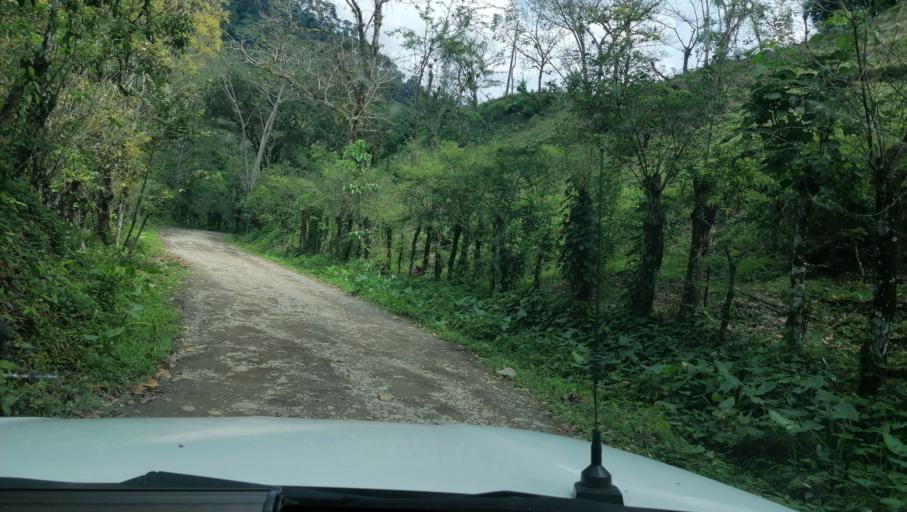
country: MX
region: Chiapas
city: Ixtacomitan
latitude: 17.4435
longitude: -93.1787
